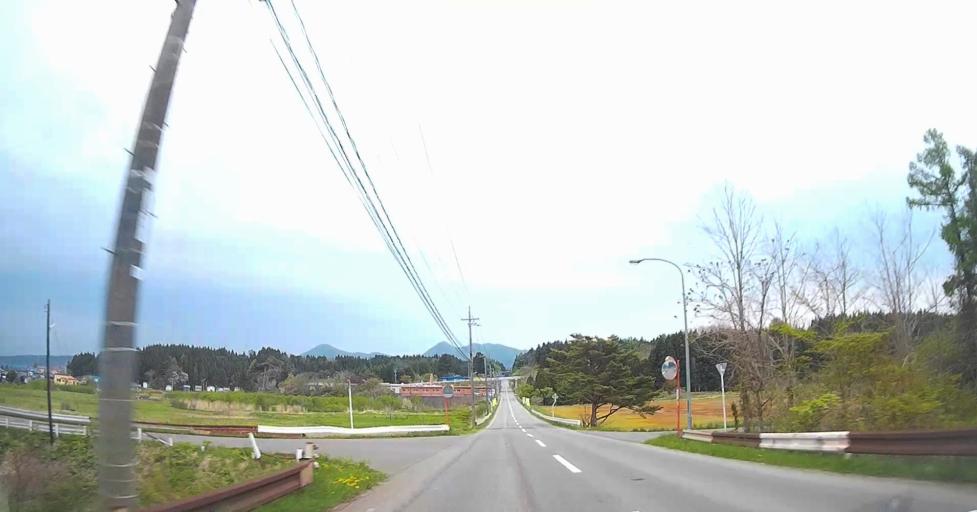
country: JP
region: Aomori
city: Goshogawara
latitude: 41.1781
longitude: 140.4759
